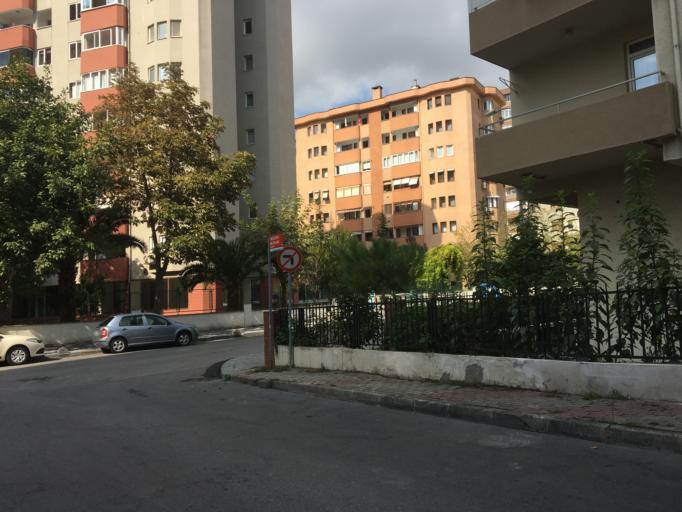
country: TR
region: Istanbul
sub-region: Atasehir
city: Atasehir
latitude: 40.9662
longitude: 29.0973
